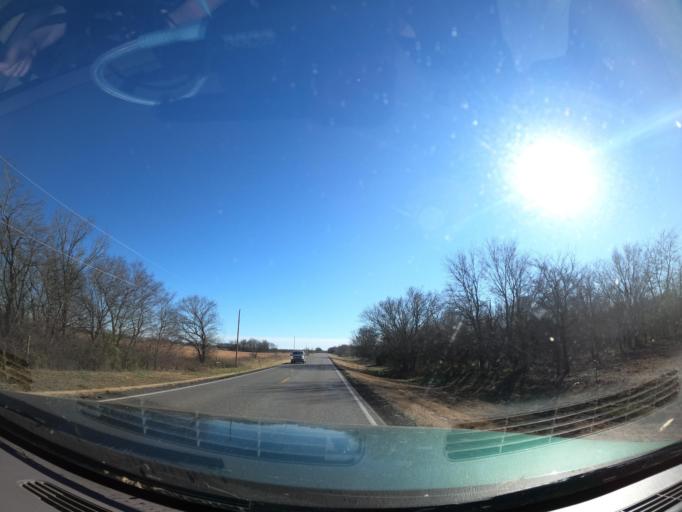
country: US
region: Oklahoma
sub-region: McIntosh County
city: Checotah
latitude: 35.5715
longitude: -95.6574
